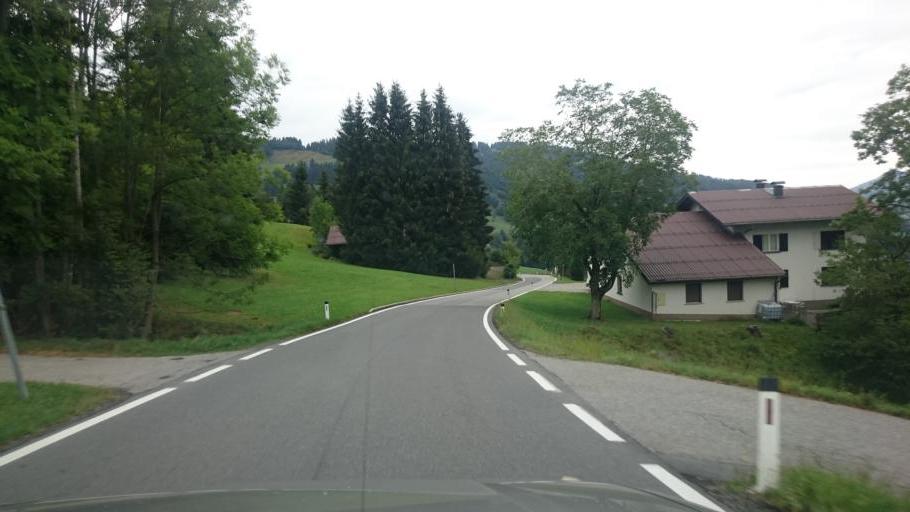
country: AT
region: Vorarlberg
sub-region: Politischer Bezirk Bregenz
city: Andelsbuch
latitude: 47.4152
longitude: 9.8386
